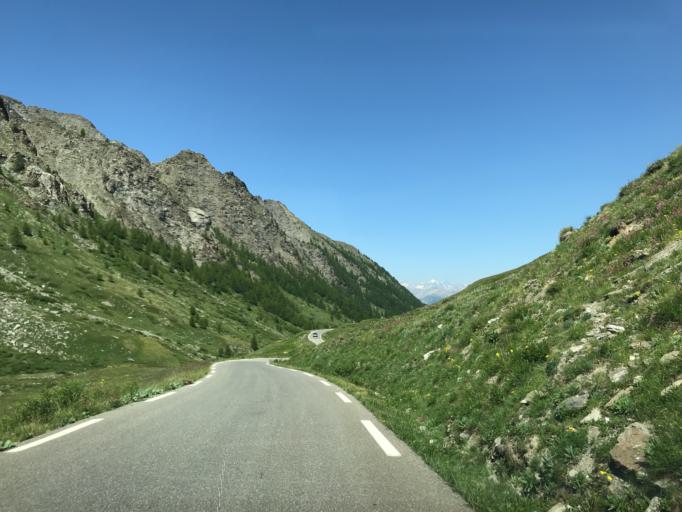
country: IT
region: Piedmont
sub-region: Provincia di Cuneo
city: Pontechianale
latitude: 44.6994
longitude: 6.9447
